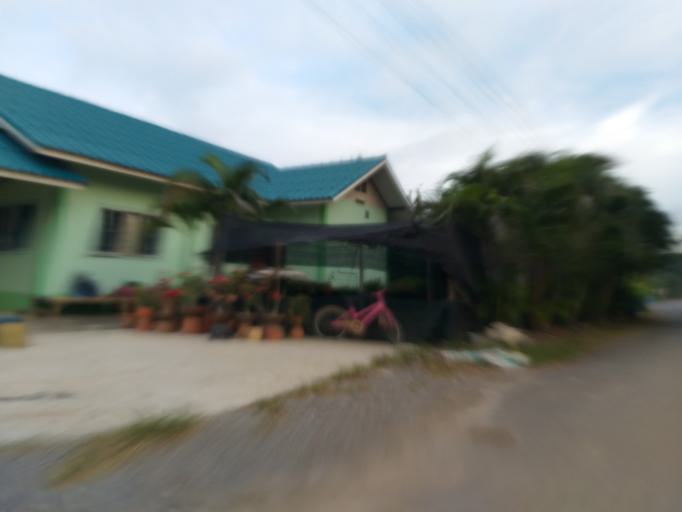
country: TH
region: Pathum Thani
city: Ban Lam Luk Ka
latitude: 14.0046
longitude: 100.7984
